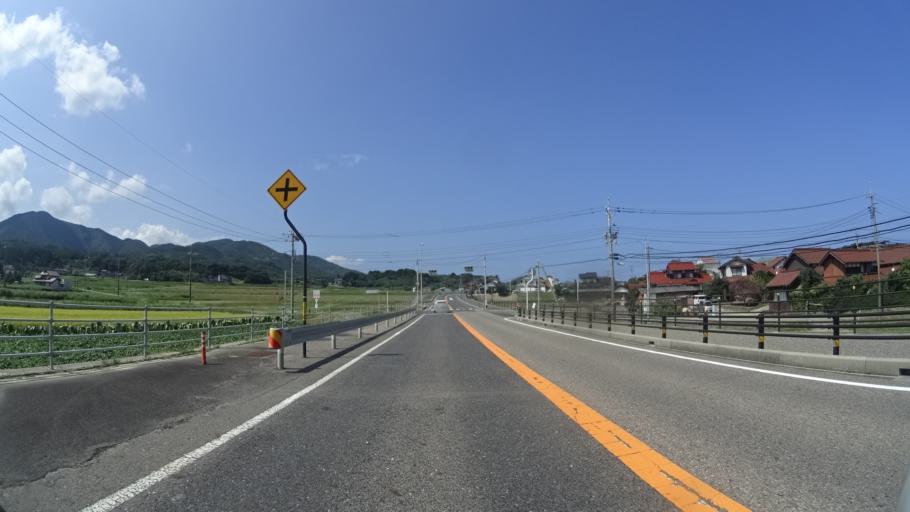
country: JP
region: Shimane
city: Masuda
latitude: 34.6710
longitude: 131.7437
